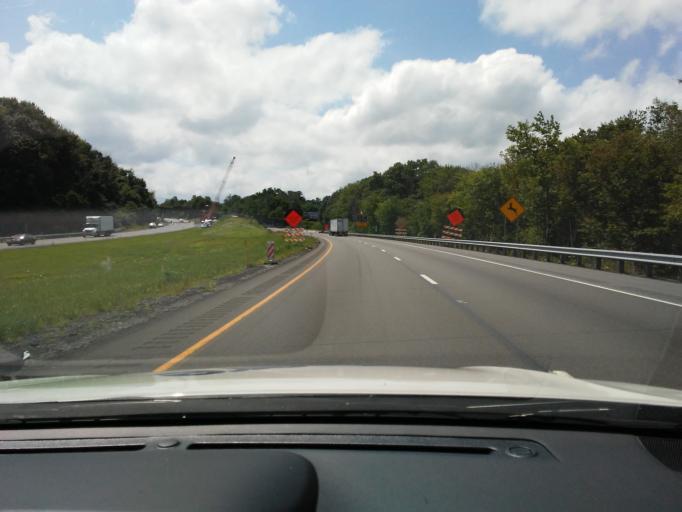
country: US
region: Pennsylvania
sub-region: Clarion County
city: Knox
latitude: 41.2004
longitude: -79.4890
